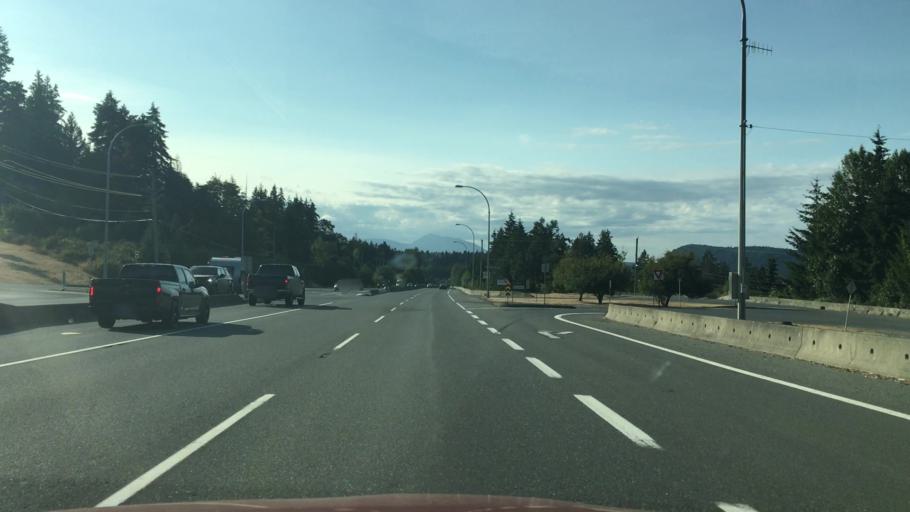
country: CA
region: British Columbia
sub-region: Cowichan Valley Regional District
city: Ladysmith
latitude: 48.9682
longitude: -123.7896
